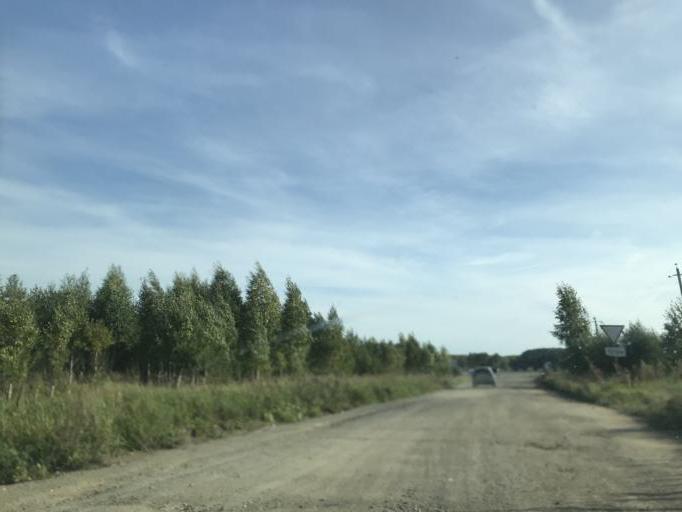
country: RU
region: Chelyabinsk
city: Poletayevo
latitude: 54.9737
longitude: 60.9706
